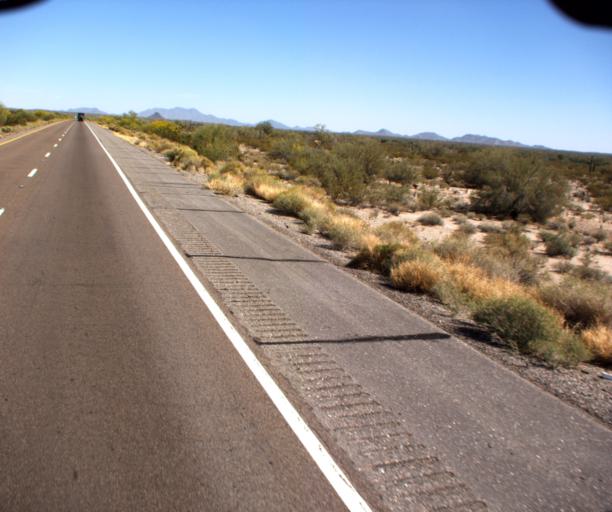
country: US
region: Arizona
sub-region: Maricopa County
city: Gila Bend
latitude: 32.8546
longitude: -112.3732
